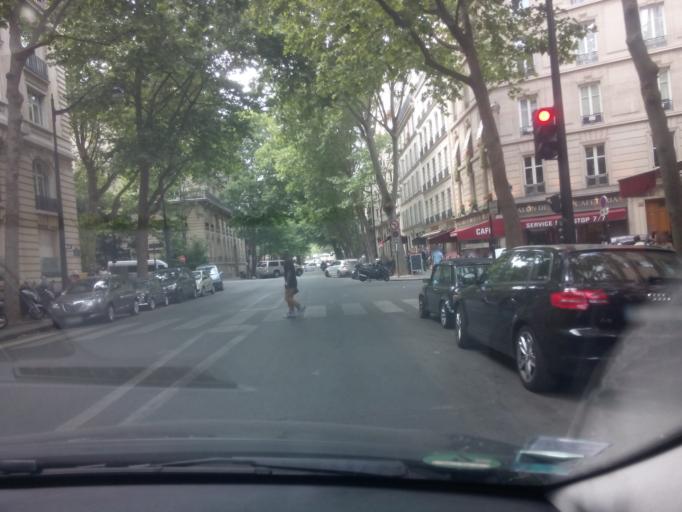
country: FR
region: Ile-de-France
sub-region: Departement des Hauts-de-Seine
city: Vanves
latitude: 48.8587
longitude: 2.2981
